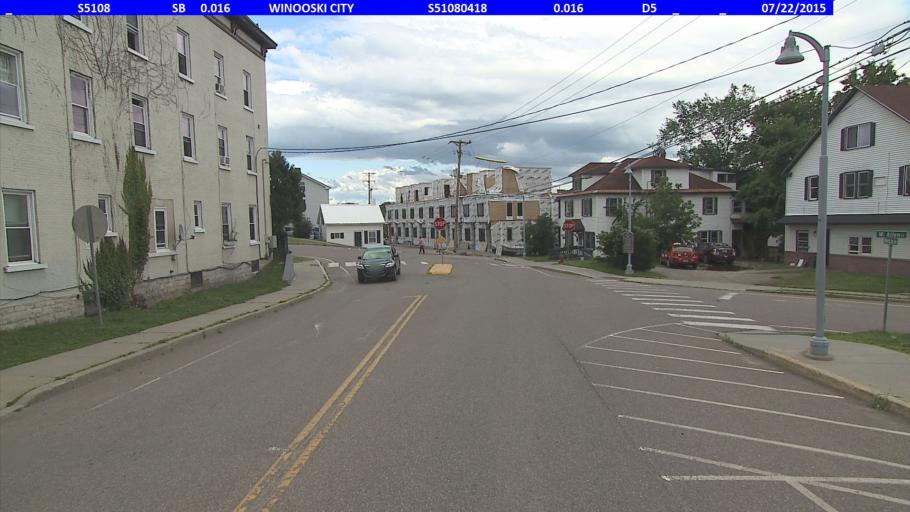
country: US
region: Vermont
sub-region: Chittenden County
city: Winooski
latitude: 44.4917
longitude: -73.1893
